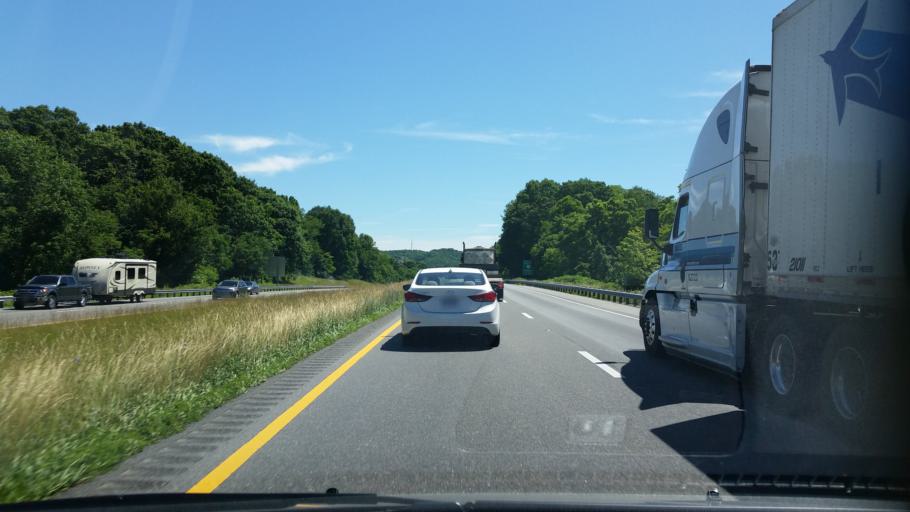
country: US
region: Virginia
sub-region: Smyth County
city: Atkins
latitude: 36.8559
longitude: -81.4624
